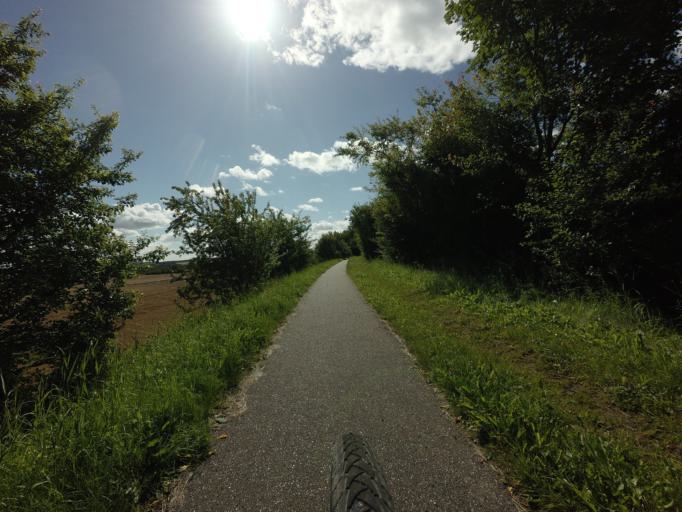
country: DK
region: Central Jutland
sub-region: Horsens Kommune
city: Braedstrup
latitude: 55.9835
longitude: 9.6883
